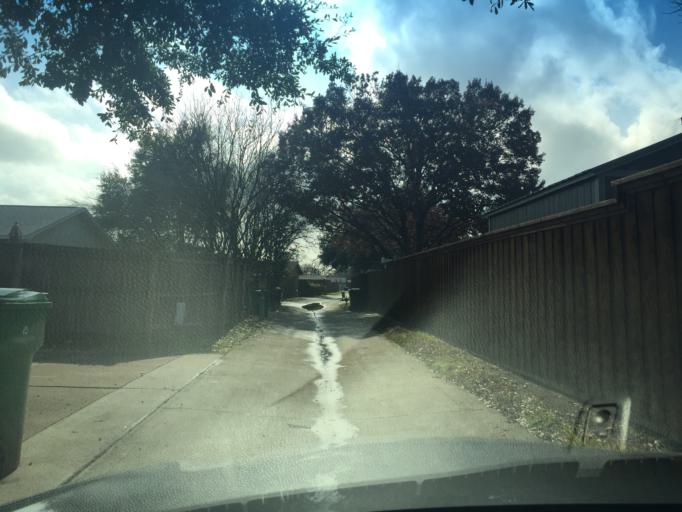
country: US
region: Texas
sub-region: Dallas County
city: Carrollton
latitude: 33.0006
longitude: -96.8794
